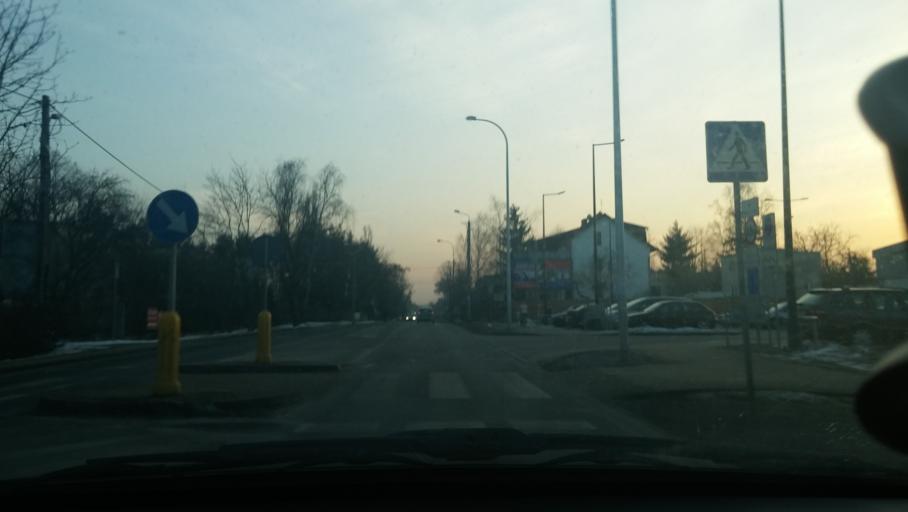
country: PL
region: Masovian Voivodeship
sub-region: Warszawa
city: Rembertow
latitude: 52.2231
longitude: 21.1389
